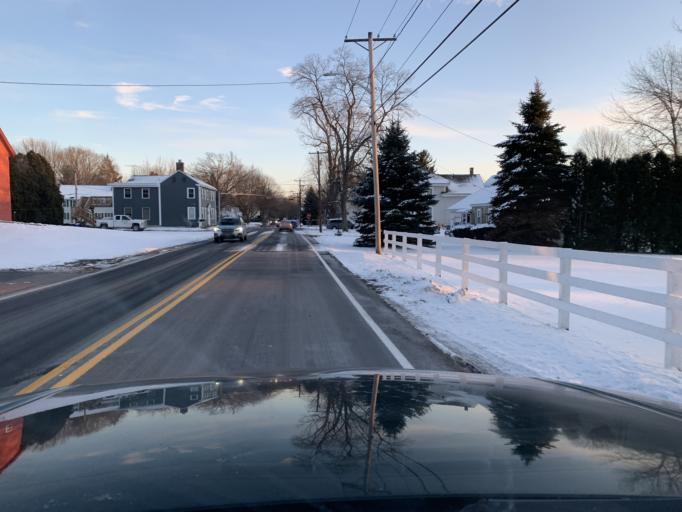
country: US
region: Massachusetts
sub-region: Essex County
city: Haverhill
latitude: 42.7869
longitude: -71.1105
